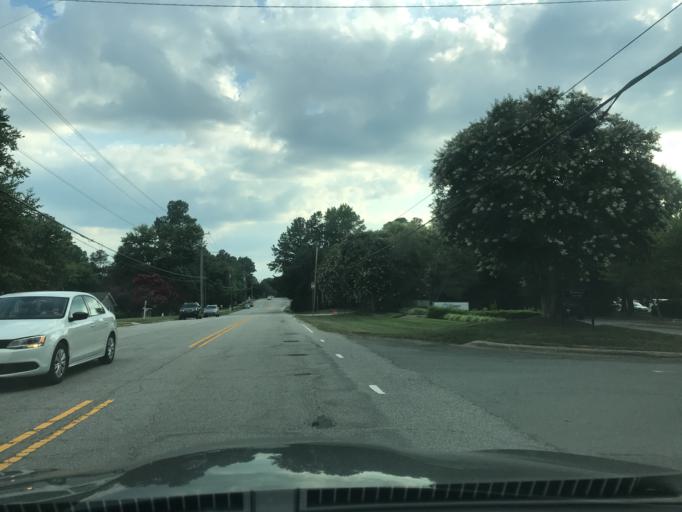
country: US
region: North Carolina
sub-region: Wake County
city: West Raleigh
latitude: 35.8250
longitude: -78.6979
